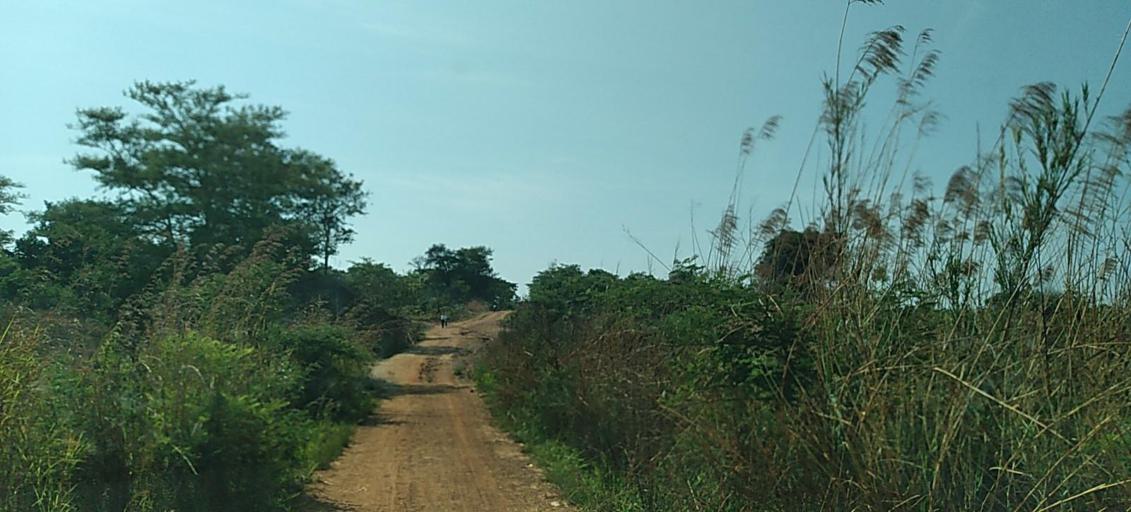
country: ZM
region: Copperbelt
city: Luanshya
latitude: -13.1924
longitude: 28.4799
